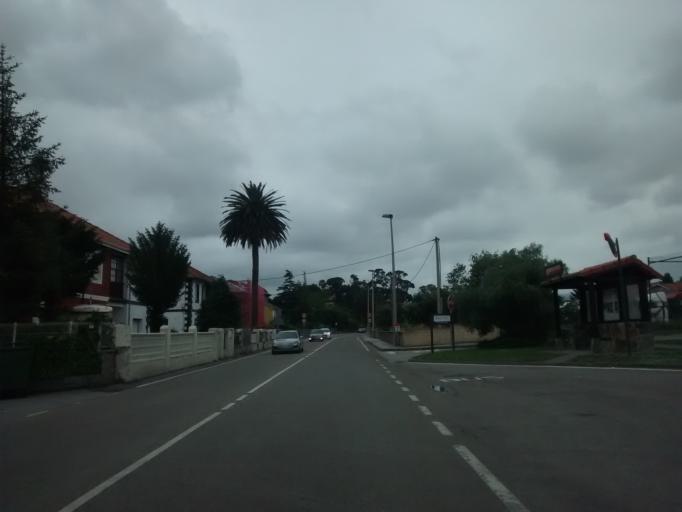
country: ES
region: Cantabria
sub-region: Provincia de Cantabria
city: Polanco
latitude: 43.3868
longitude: -4.0465
